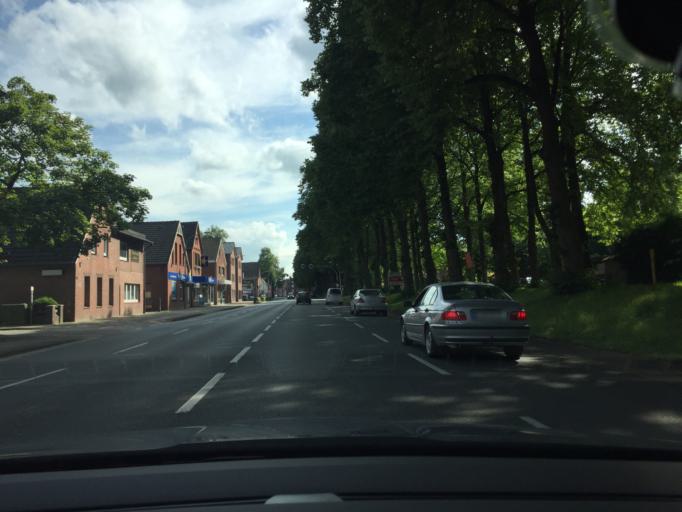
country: DE
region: Lower Saxony
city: Aurich
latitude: 53.4790
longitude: 7.4878
